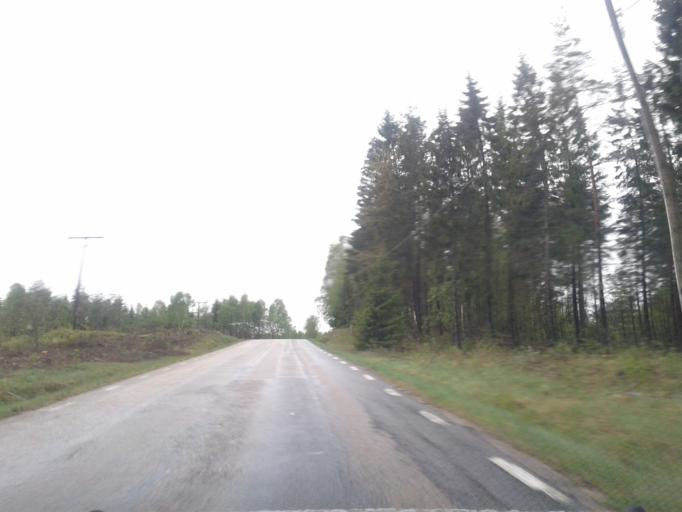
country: SE
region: Vaestra Goetaland
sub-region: Lilla Edets Kommun
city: Lodose
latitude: 58.0765
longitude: 12.0303
